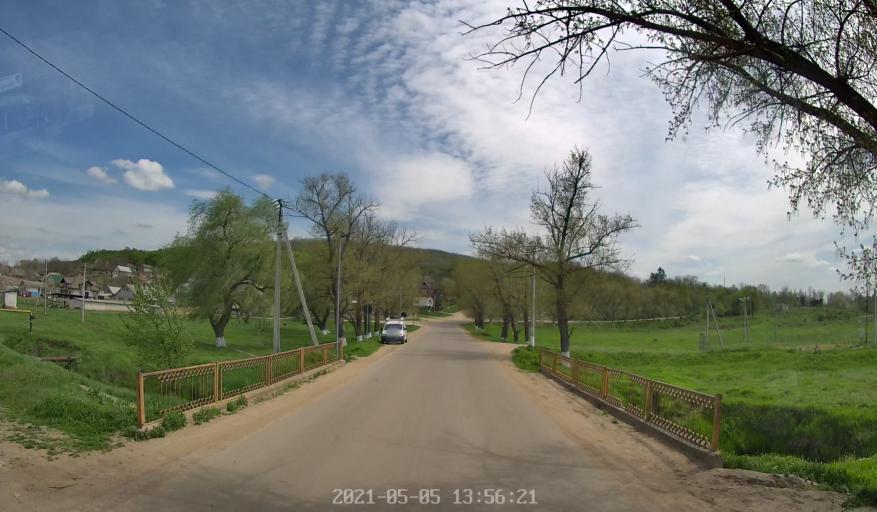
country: MD
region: Chisinau
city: Vadul lui Voda
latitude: 47.0632
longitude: 29.1320
